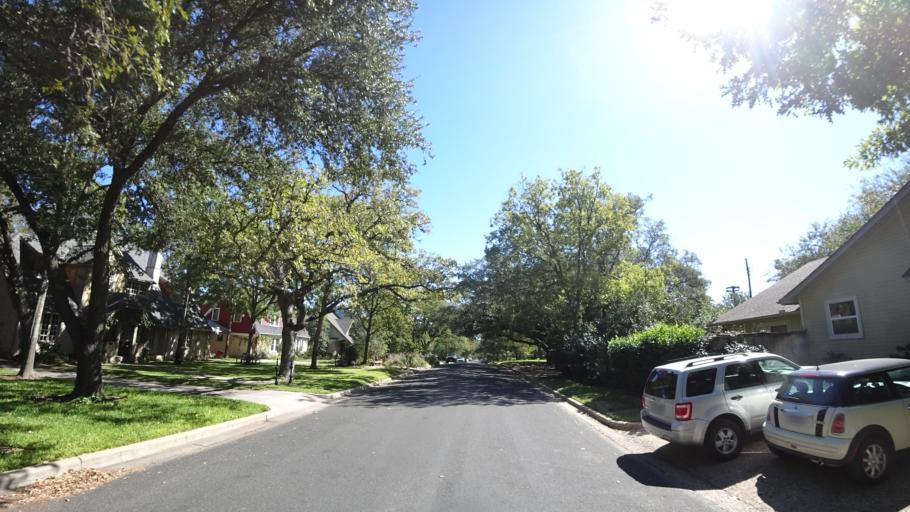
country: US
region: Texas
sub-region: Travis County
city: Rollingwood
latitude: 30.2985
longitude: -97.7646
